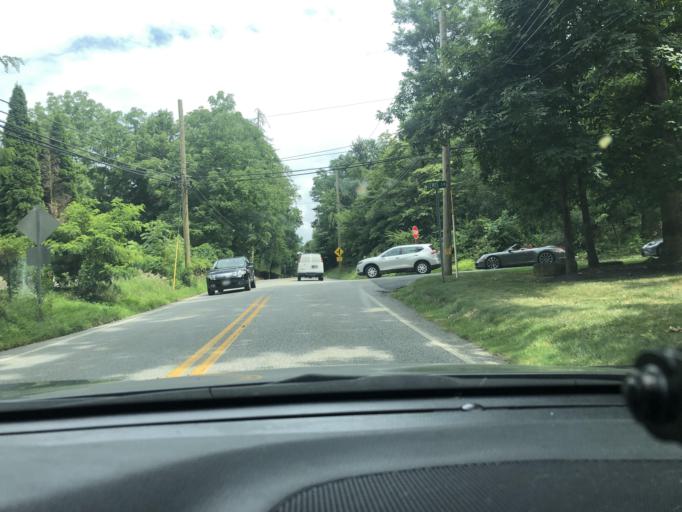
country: US
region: Pennsylvania
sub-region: Montgomery County
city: Ambler
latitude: 40.1554
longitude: -75.2407
